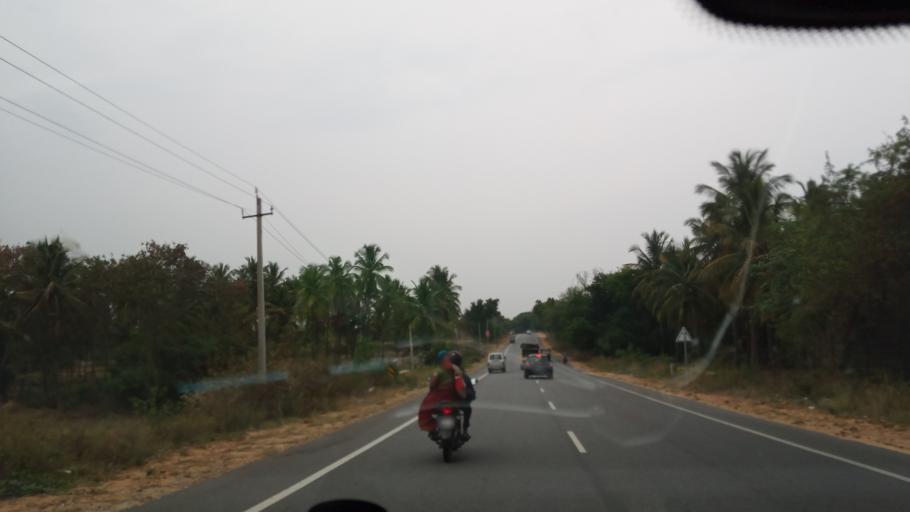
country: IN
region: Karnataka
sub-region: Mandya
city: Belluru
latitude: 12.9390
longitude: 76.7508
